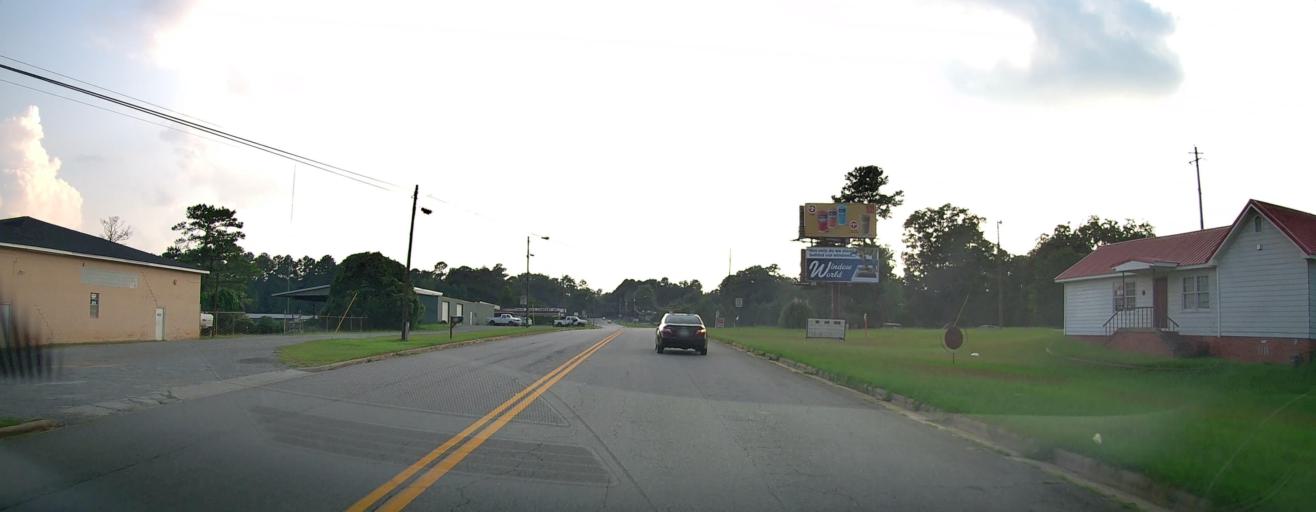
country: US
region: Georgia
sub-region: Jones County
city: Gray
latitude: 33.0144
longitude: -83.5223
